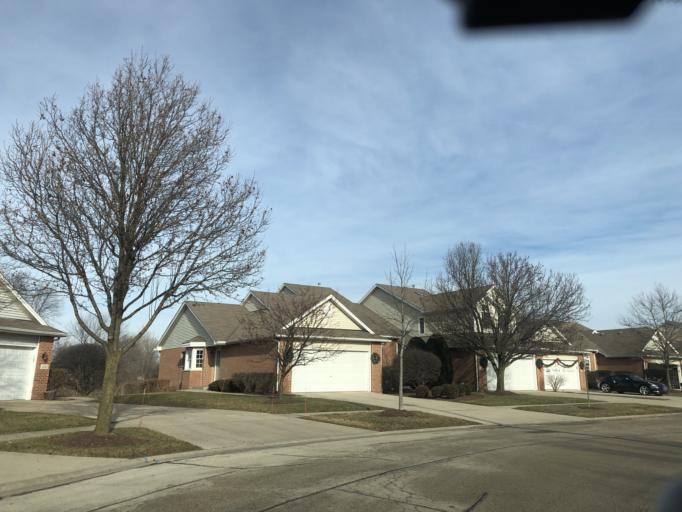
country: US
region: Illinois
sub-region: DuPage County
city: Woodridge
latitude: 41.7211
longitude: -88.0293
